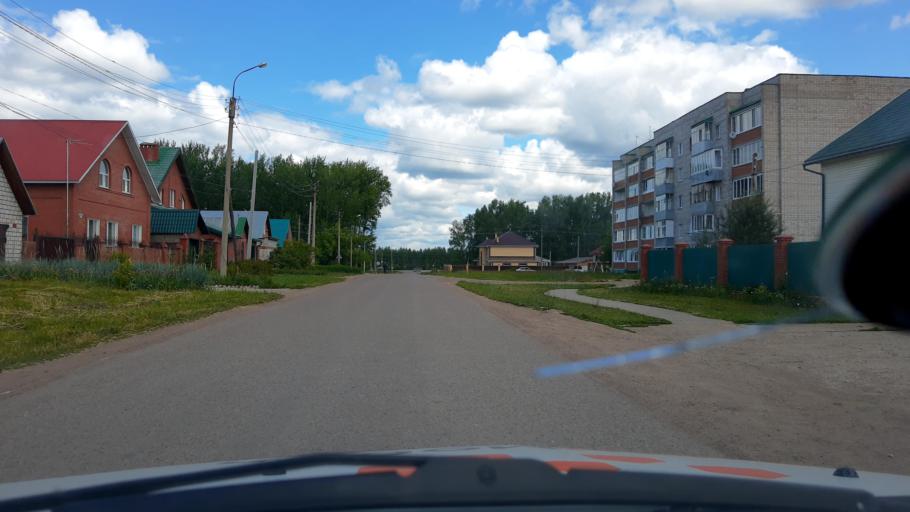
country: RU
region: Bashkortostan
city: Blagoveshchensk
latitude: 55.0507
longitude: 55.9661
